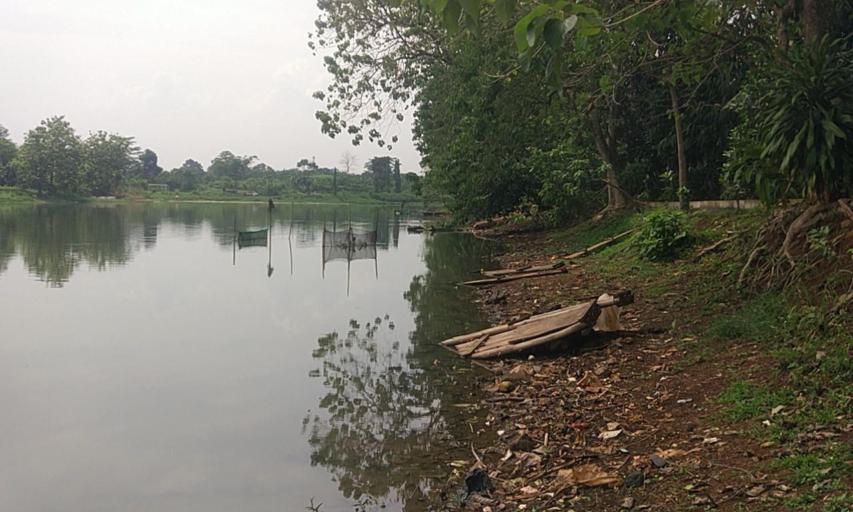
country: ID
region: West Java
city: Ciampea
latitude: -6.4954
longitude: 106.7429
